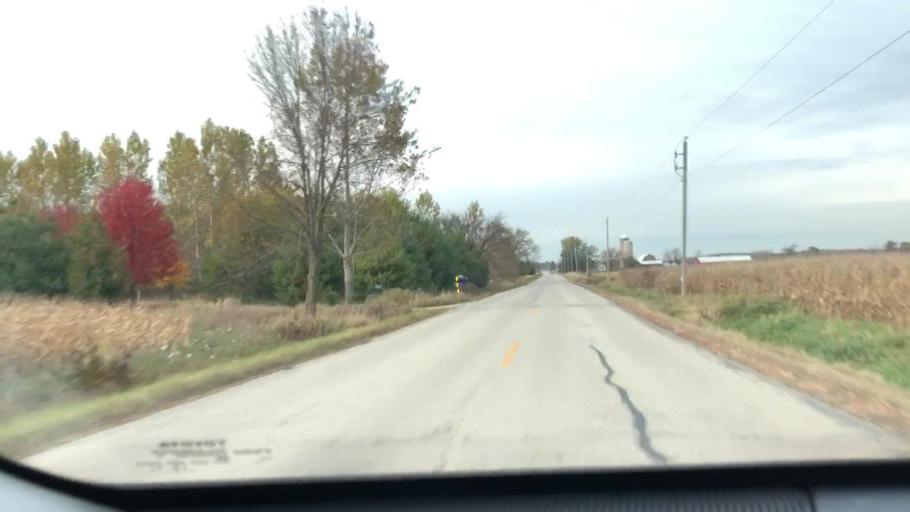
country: US
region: Wisconsin
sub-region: Outagamie County
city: Seymour
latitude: 44.4542
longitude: -88.3500
